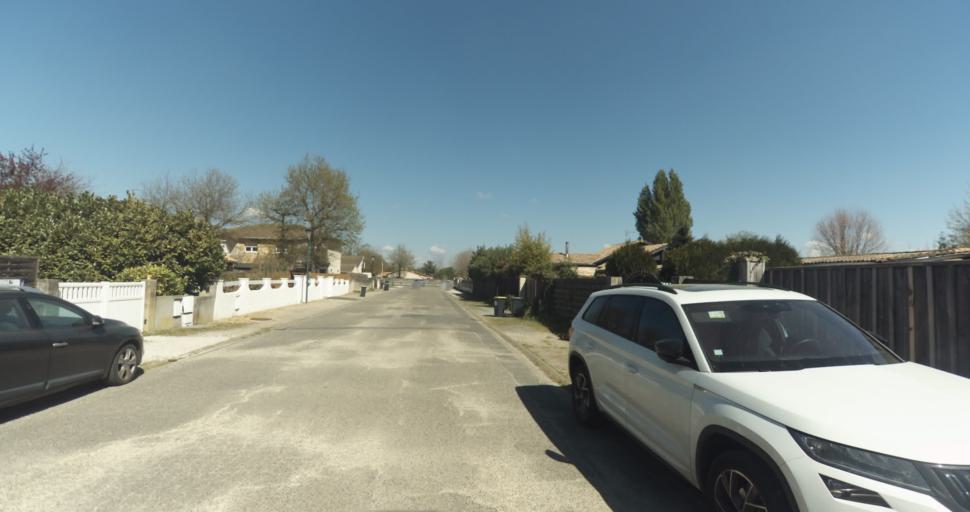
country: FR
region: Aquitaine
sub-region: Departement de la Gironde
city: Martignas-sur-Jalle
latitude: 44.8068
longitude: -0.7893
